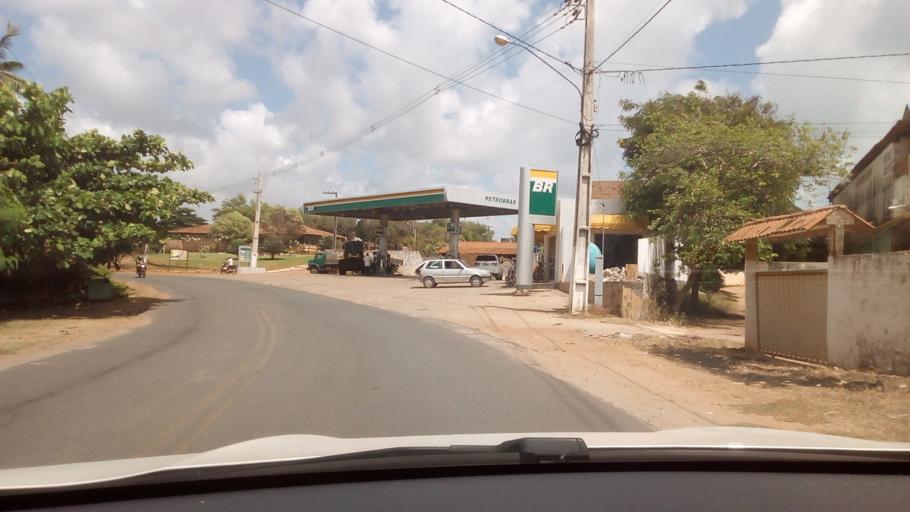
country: BR
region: Paraiba
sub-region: Conde
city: Conde
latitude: -7.2788
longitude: -34.8008
